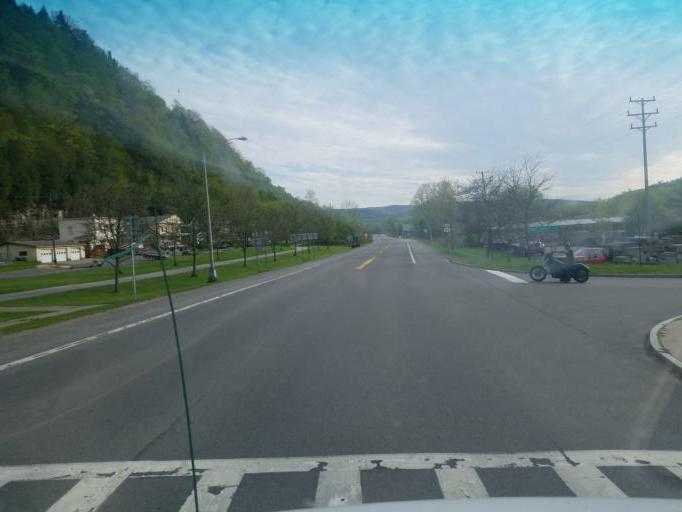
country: US
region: New York
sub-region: Herkimer County
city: Little Falls
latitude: 43.0368
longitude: -74.8614
